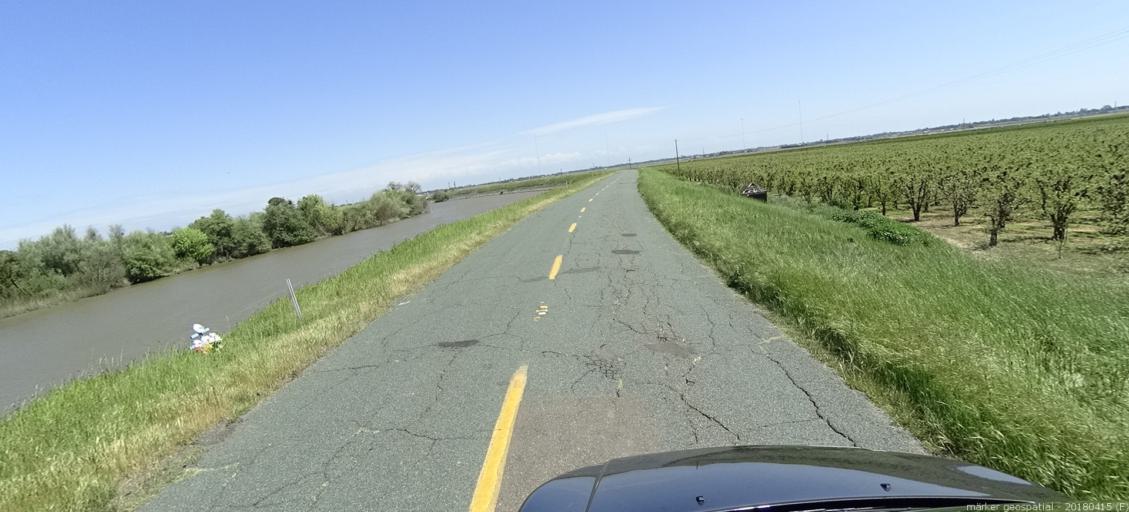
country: US
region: California
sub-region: Sacramento County
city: Walnut Grove
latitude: 38.2617
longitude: -121.5921
